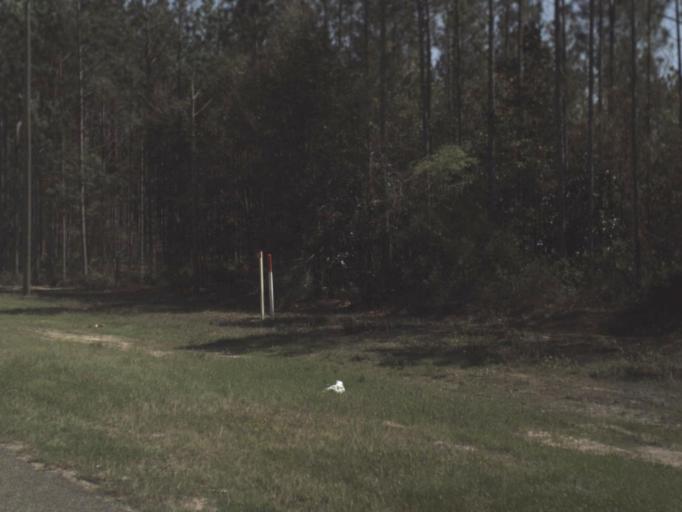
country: US
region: Florida
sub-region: Liberty County
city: Bristol
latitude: 30.4188
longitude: -84.8874
